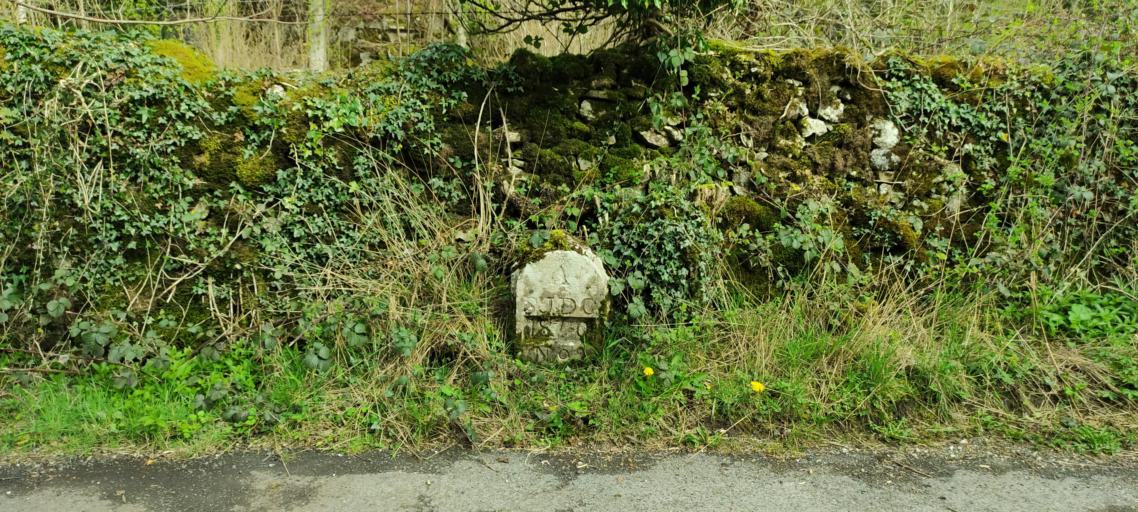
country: GB
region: England
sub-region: Cumbria
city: Arnside
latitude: 54.2123
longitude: -2.8009
